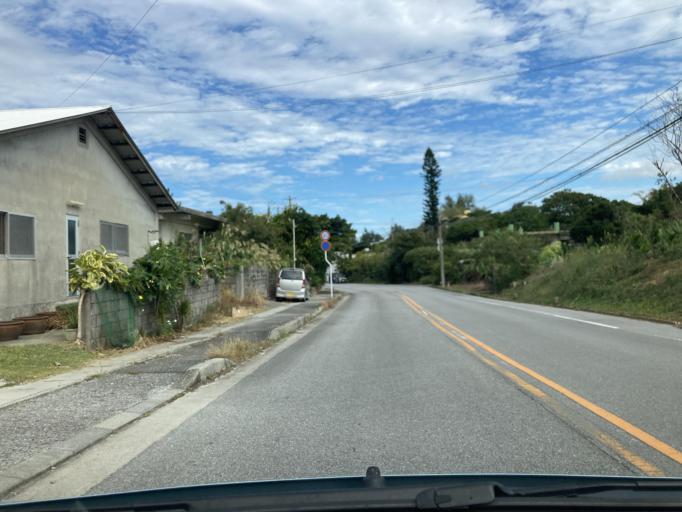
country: JP
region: Okinawa
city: Ishikawa
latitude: 26.4356
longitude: 127.7778
